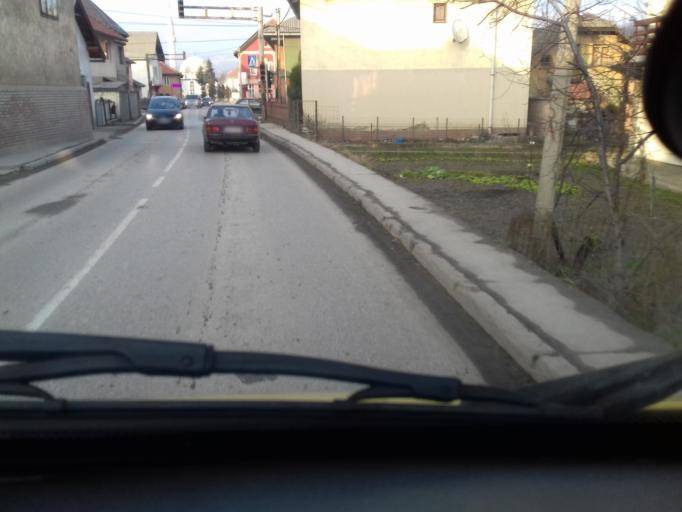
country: BA
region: Federation of Bosnia and Herzegovina
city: Kakanj
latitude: 44.1128
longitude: 18.1176
